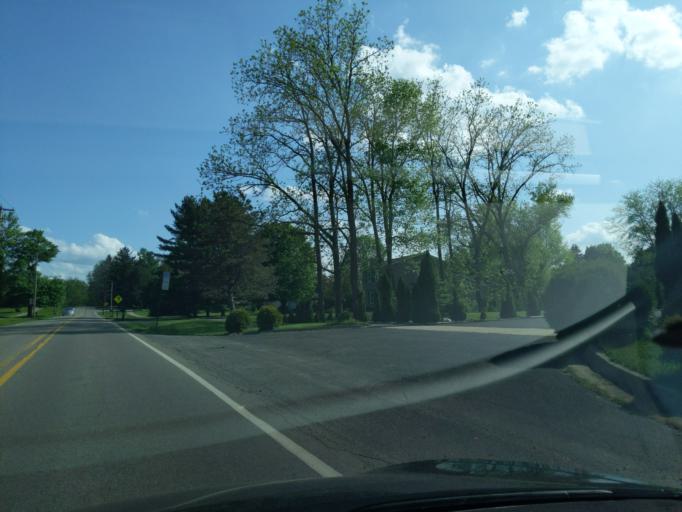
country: US
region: Michigan
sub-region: Ingham County
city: Okemos
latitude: 42.6954
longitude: -84.4104
